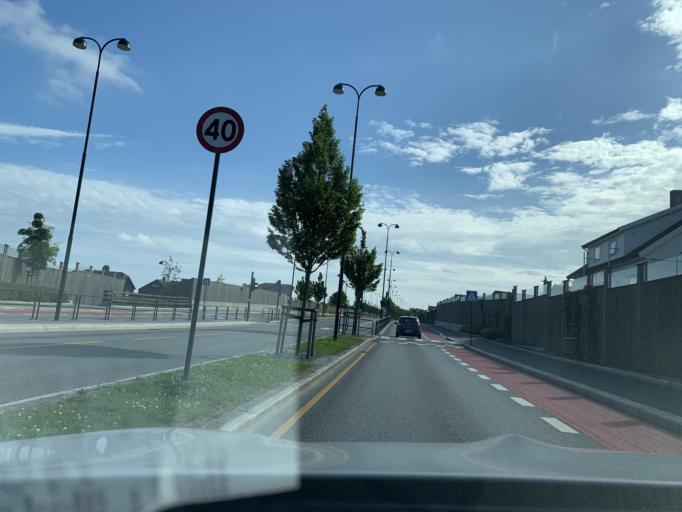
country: NO
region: Rogaland
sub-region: Stavanger
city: Stavanger
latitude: 58.9316
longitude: 5.7383
